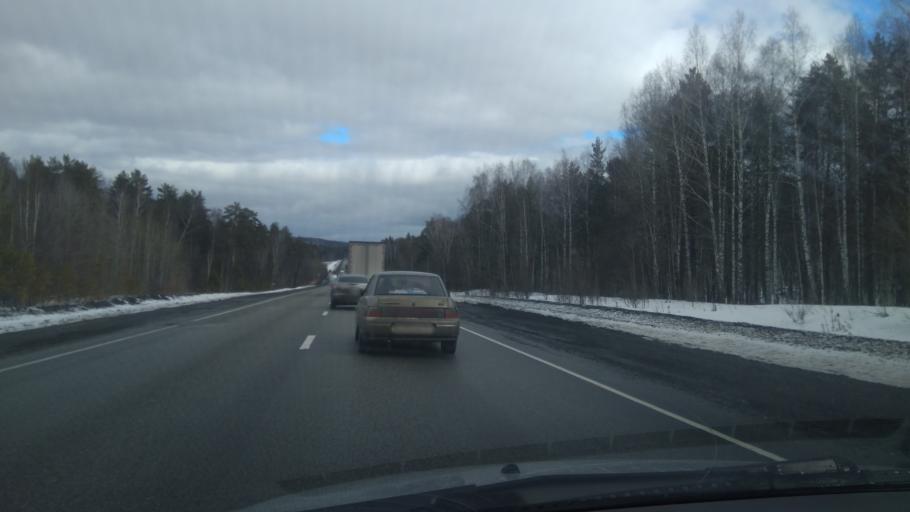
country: RU
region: Sverdlovsk
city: Bisert'
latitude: 56.8187
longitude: 58.7544
